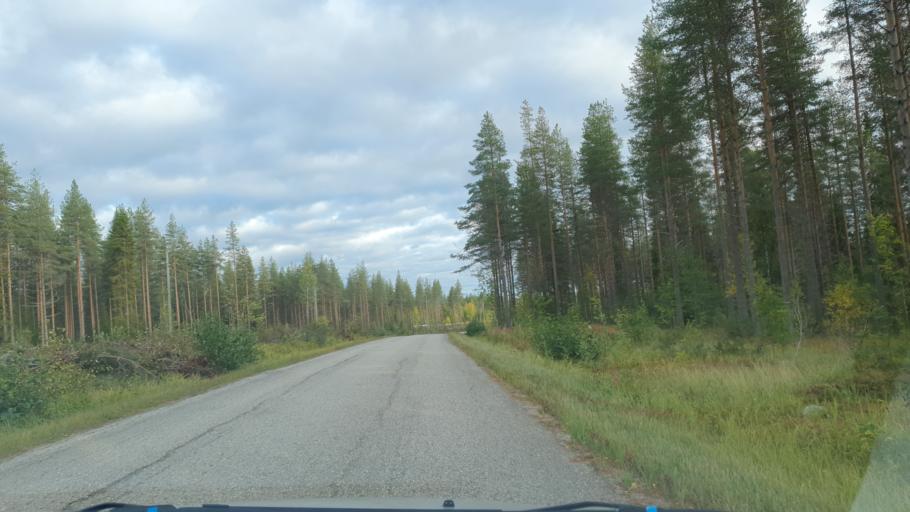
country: FI
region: North Karelia
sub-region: Pielisen Karjala
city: Lieksa
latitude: 63.9210
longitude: 30.1552
